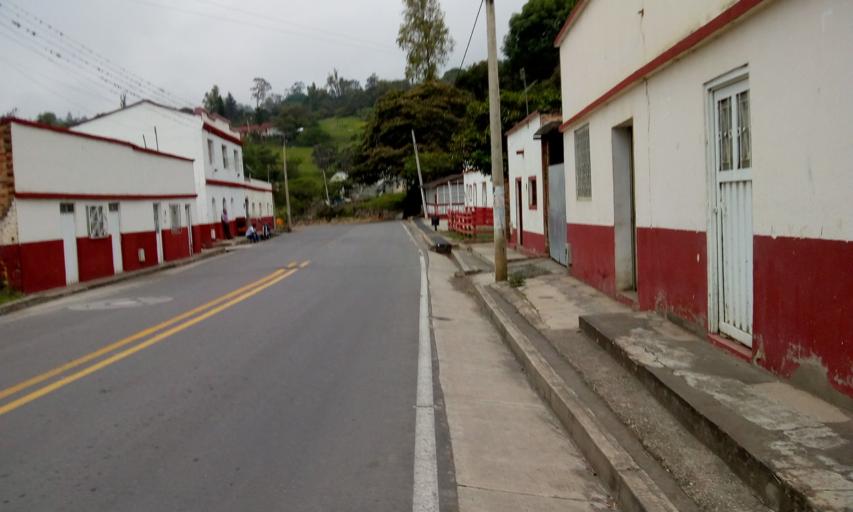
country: CO
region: Boyaca
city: Tipacoque
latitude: 6.4161
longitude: -72.6918
